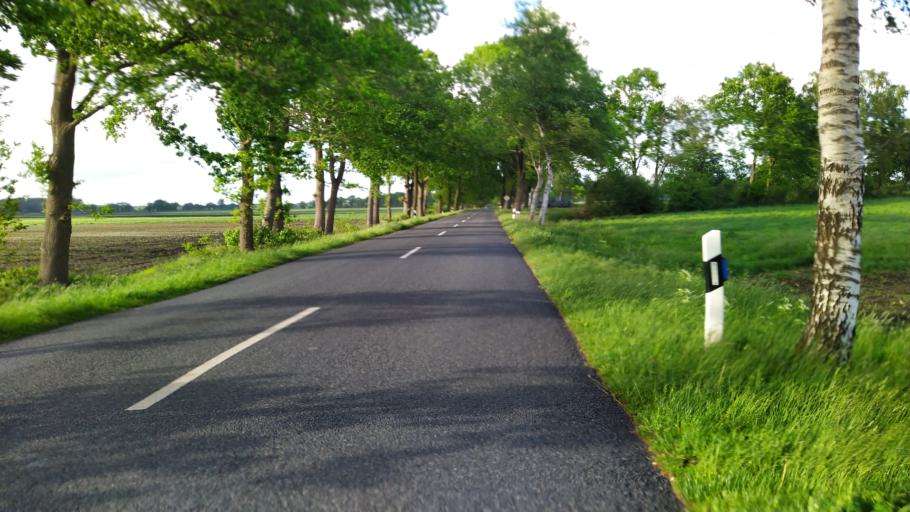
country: DE
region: Lower Saxony
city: Farven
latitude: 53.4540
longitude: 9.2791
